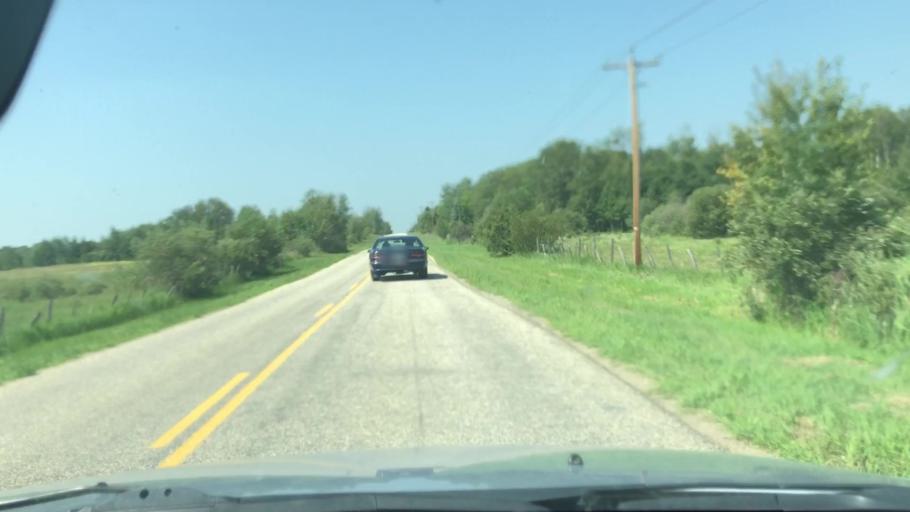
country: CA
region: Alberta
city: Devon
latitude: 53.4253
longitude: -113.8005
